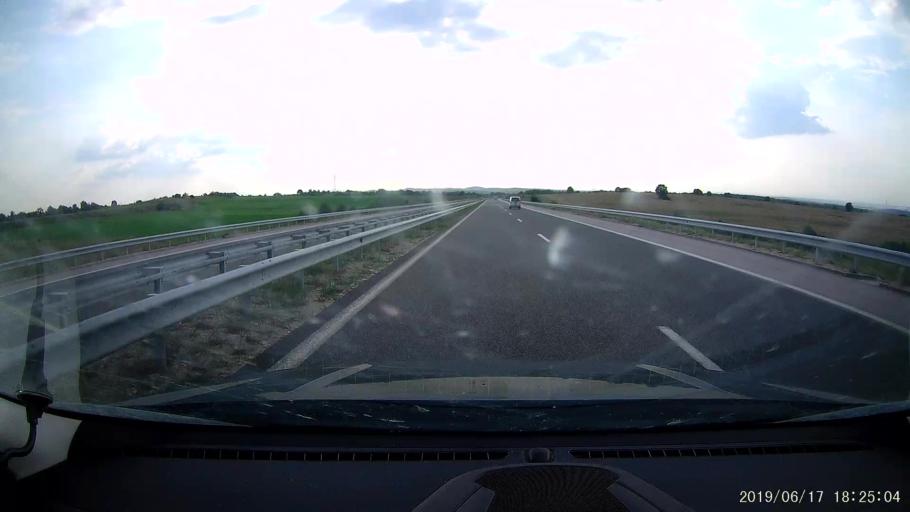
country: BG
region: Khaskovo
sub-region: Obshtina Dimitrovgrad
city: Dimitrovgrad
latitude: 41.9892
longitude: 25.6723
